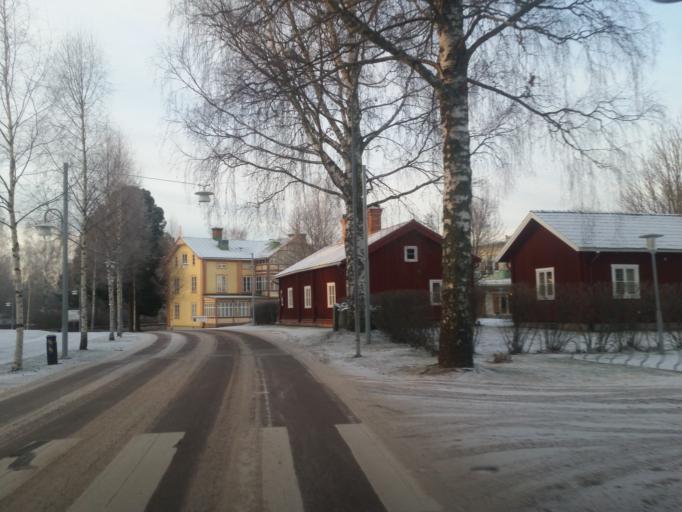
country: SE
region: Dalarna
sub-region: Leksand Municipality
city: Leksand
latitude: 60.7321
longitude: 14.9881
